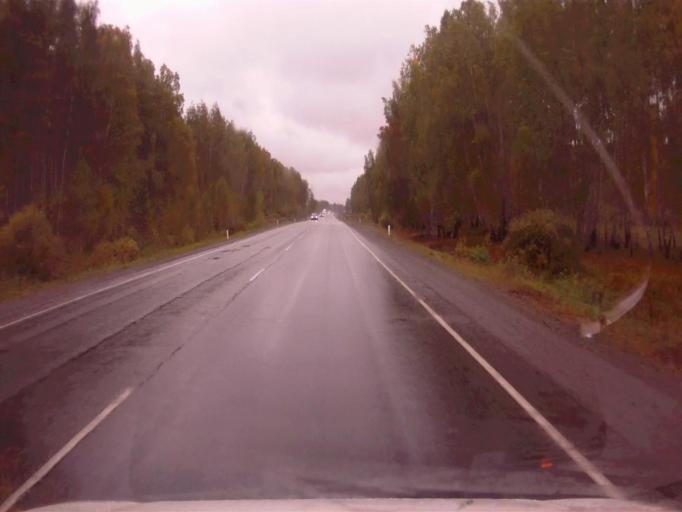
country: RU
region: Chelyabinsk
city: Argayash
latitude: 55.4650
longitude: 60.9124
